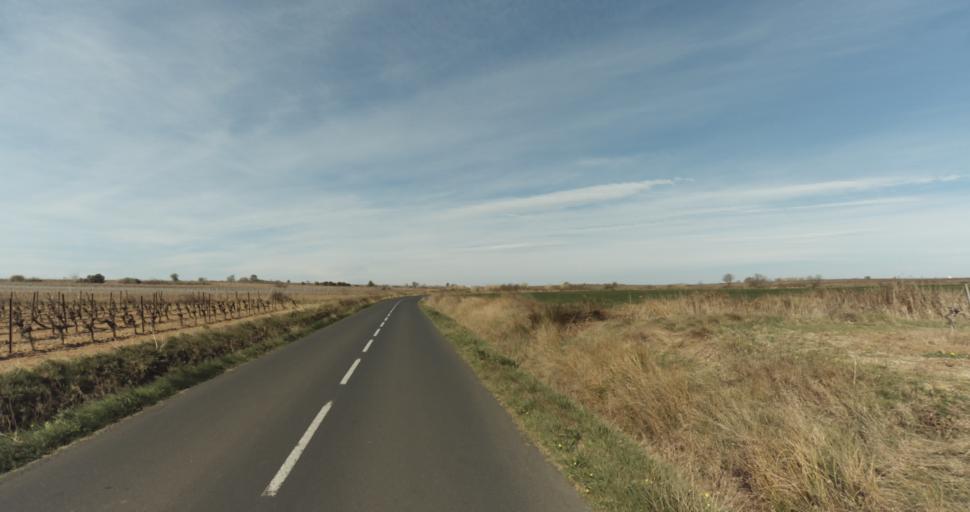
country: FR
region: Languedoc-Roussillon
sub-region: Departement de l'Herault
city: Marseillan
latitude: 43.3586
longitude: 3.5085
